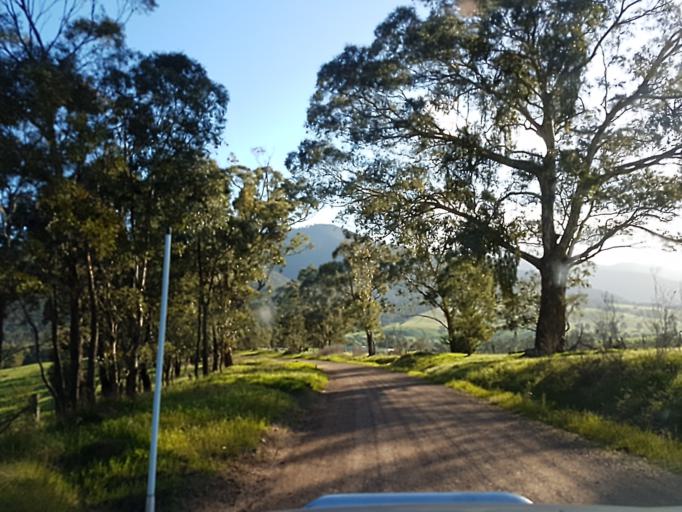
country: AU
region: Victoria
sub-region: East Gippsland
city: Bairnsdale
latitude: -37.4892
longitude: 147.1905
